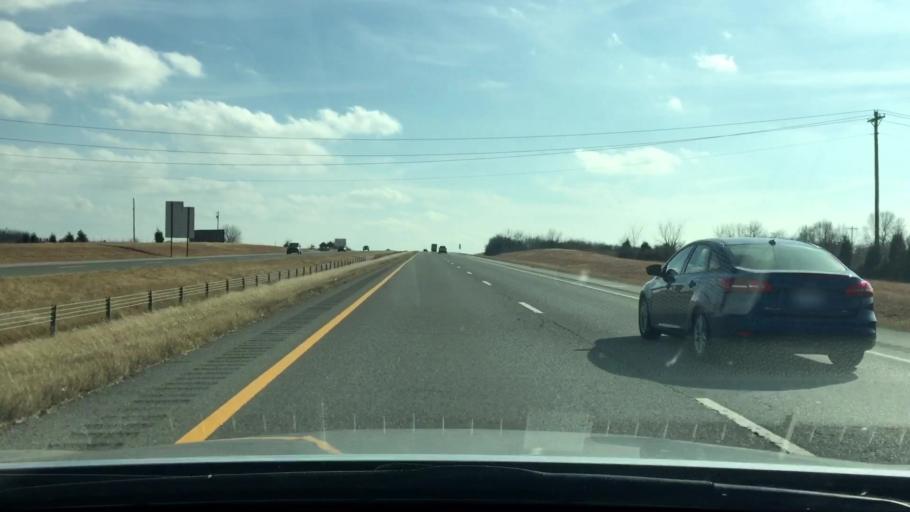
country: US
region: Oklahoma
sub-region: McClain County
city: Purcell
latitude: 34.9668
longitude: -97.3703
